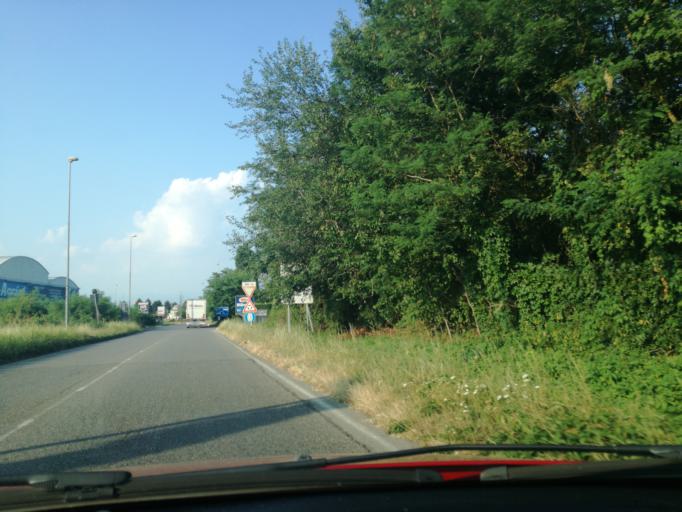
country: IT
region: Lombardy
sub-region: Provincia di Monza e Brianza
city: Velasca
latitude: 45.6408
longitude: 9.3447
